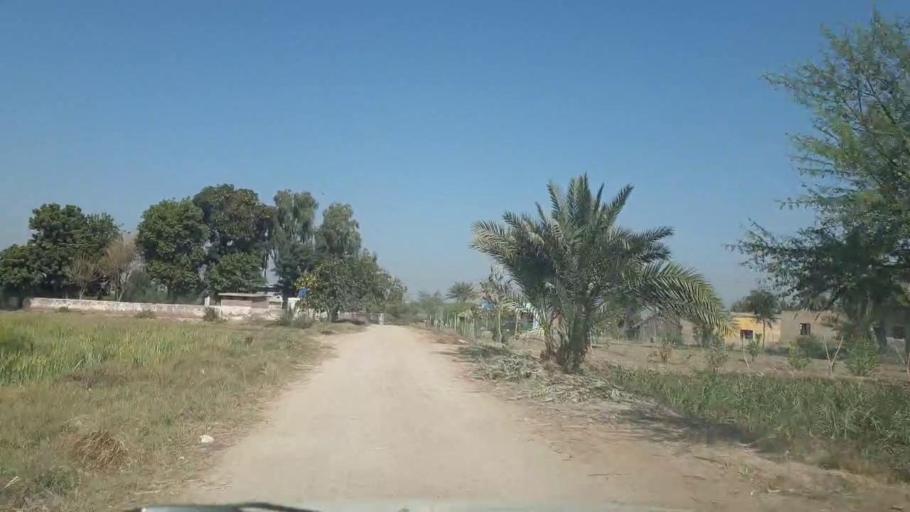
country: PK
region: Sindh
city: Mirpur Khas
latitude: 25.5192
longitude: 69.1816
